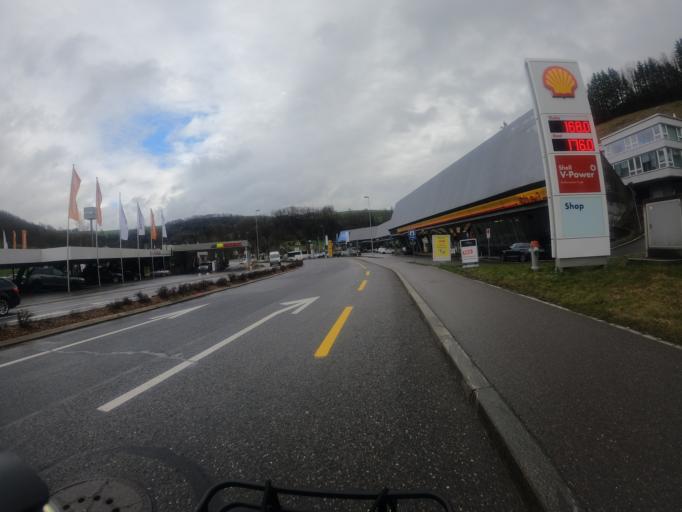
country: CH
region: Zurich
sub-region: Bezirk Horgen
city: Horgen / Oberdorf
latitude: 47.2165
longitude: 8.5758
